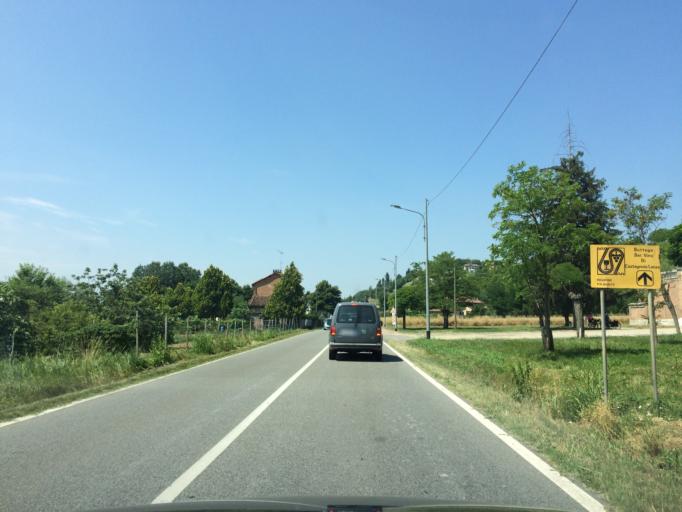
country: IT
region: Piedmont
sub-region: Provincia di Asti
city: Castagnole delle Lanze
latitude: 44.7549
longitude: 8.1603
